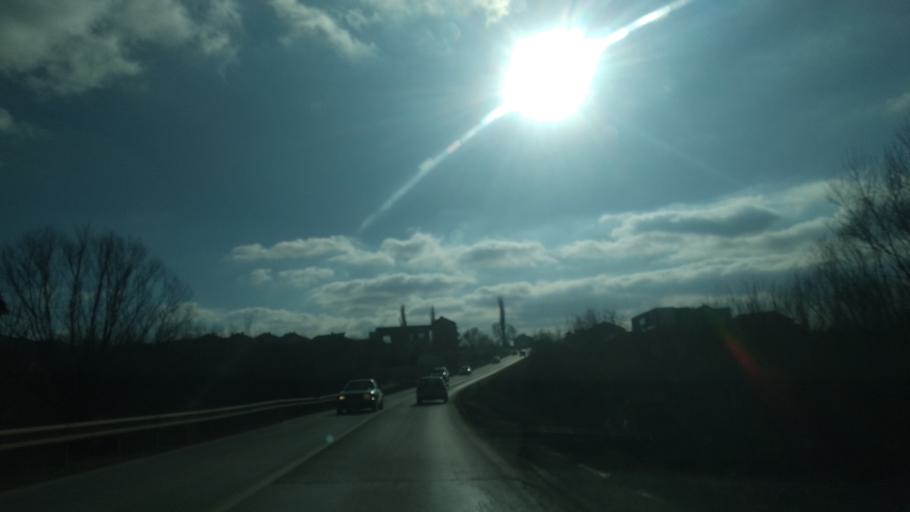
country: XK
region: Pristina
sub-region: Komuna e Prishtines
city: Pristina
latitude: 42.7400
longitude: 21.1422
